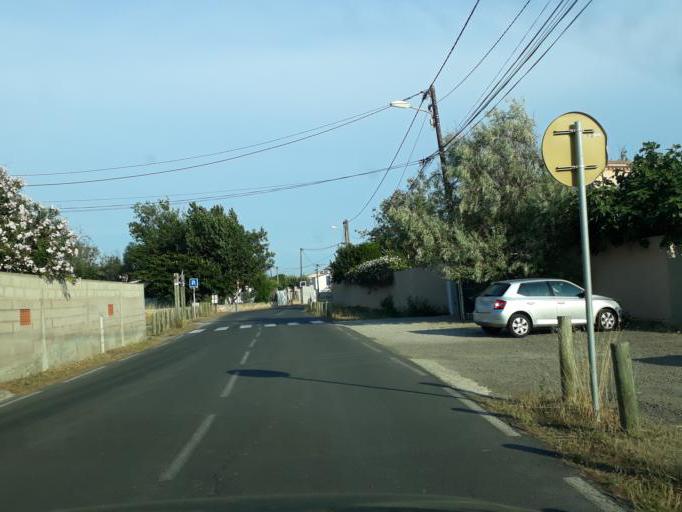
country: FR
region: Languedoc-Roussillon
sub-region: Departement de l'Herault
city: Agde
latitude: 43.2792
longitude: 3.4640
